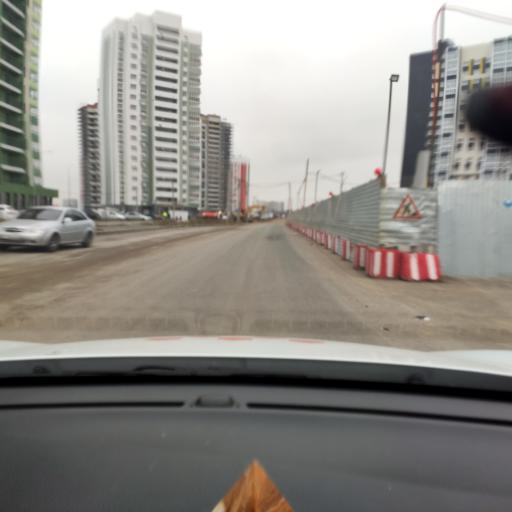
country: RU
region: Tatarstan
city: Osinovo
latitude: 55.8578
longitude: 48.9053
